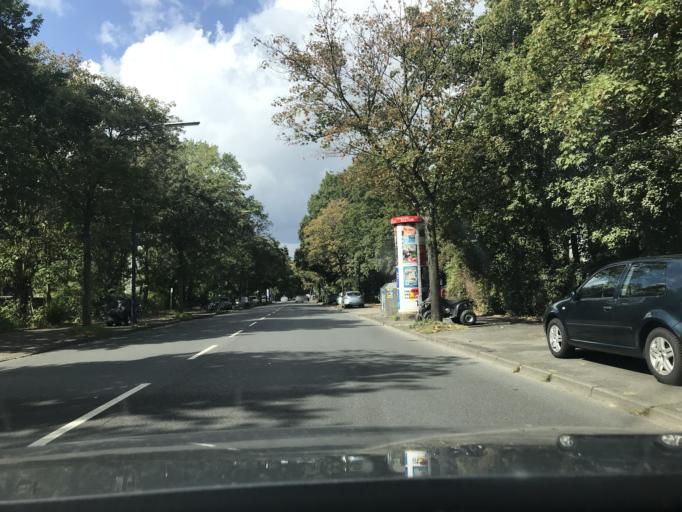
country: DE
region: North Rhine-Westphalia
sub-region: Regierungsbezirk Dusseldorf
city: Dusseldorf
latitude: 51.2424
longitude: 6.8205
